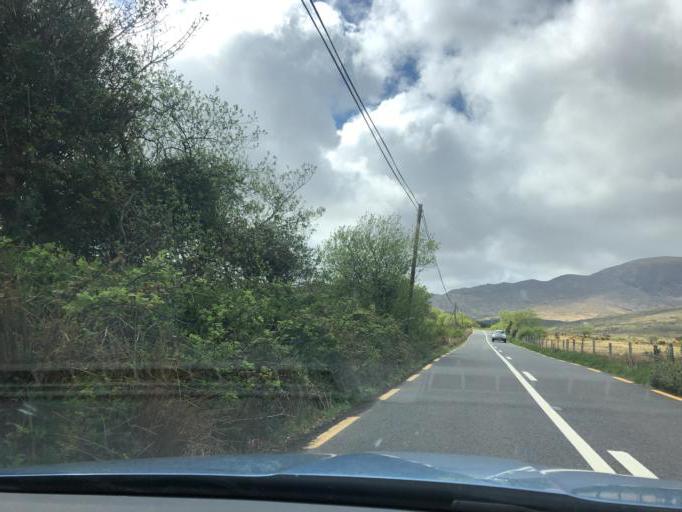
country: IE
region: Munster
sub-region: Ciarrai
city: Cahersiveen
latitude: 51.8300
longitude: -9.9424
